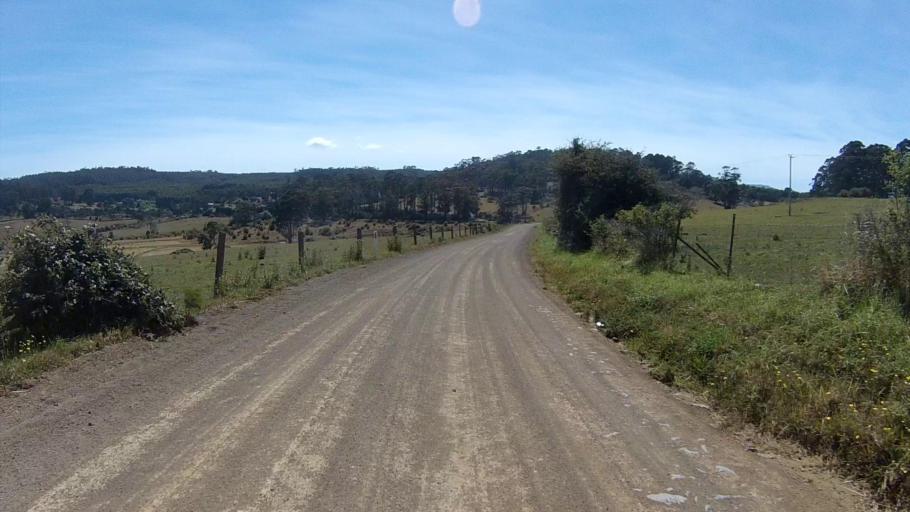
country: AU
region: Tasmania
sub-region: Sorell
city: Sorell
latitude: -42.7211
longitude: 147.7455
